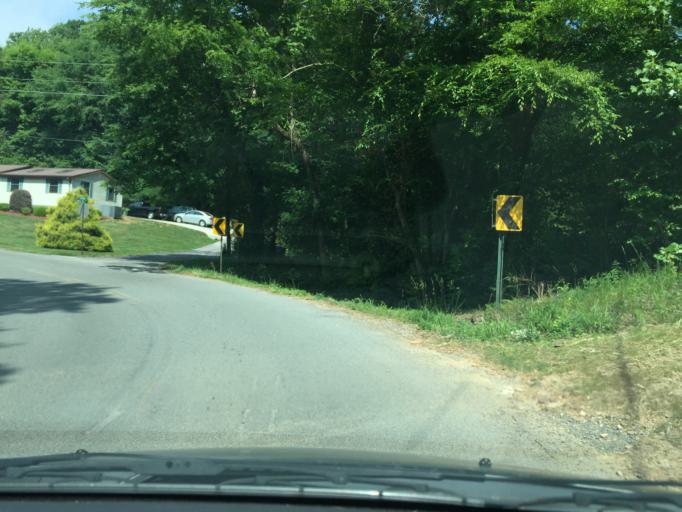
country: US
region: Tennessee
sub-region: Hamilton County
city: Collegedale
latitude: 35.0656
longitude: -85.0454
